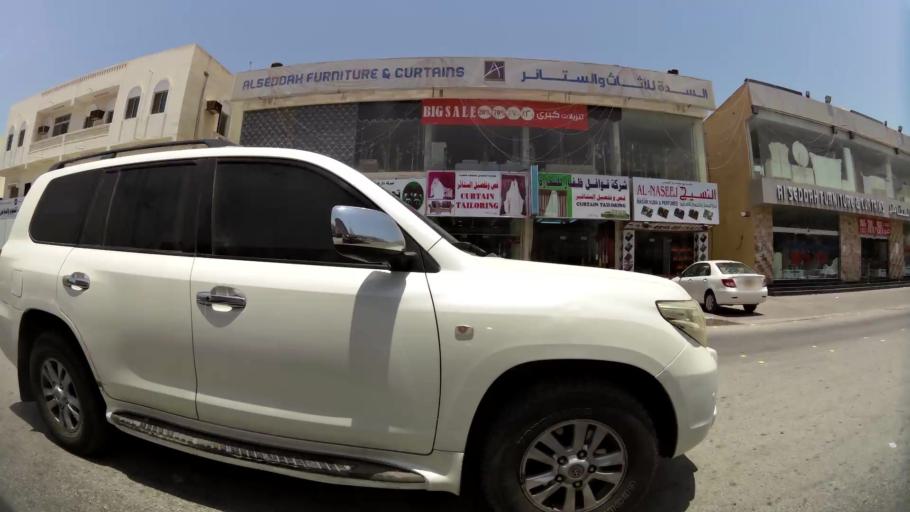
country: OM
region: Zufar
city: Salalah
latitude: 17.0140
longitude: 54.1033
